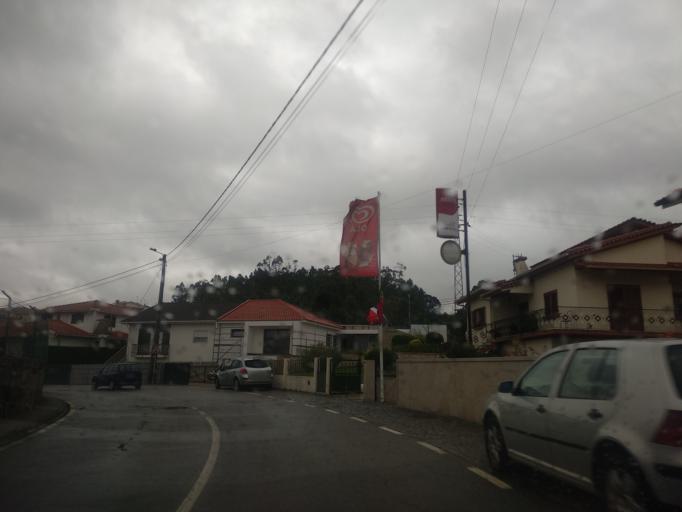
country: PT
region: Braga
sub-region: Guimaraes
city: Ponte
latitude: 41.4848
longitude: -8.3179
